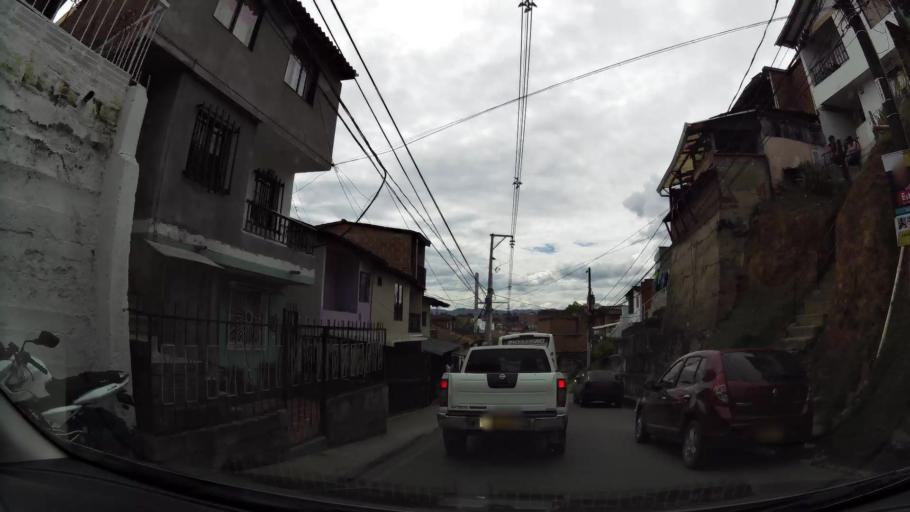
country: CO
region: Antioquia
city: Rionegro
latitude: 6.1549
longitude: -75.3662
